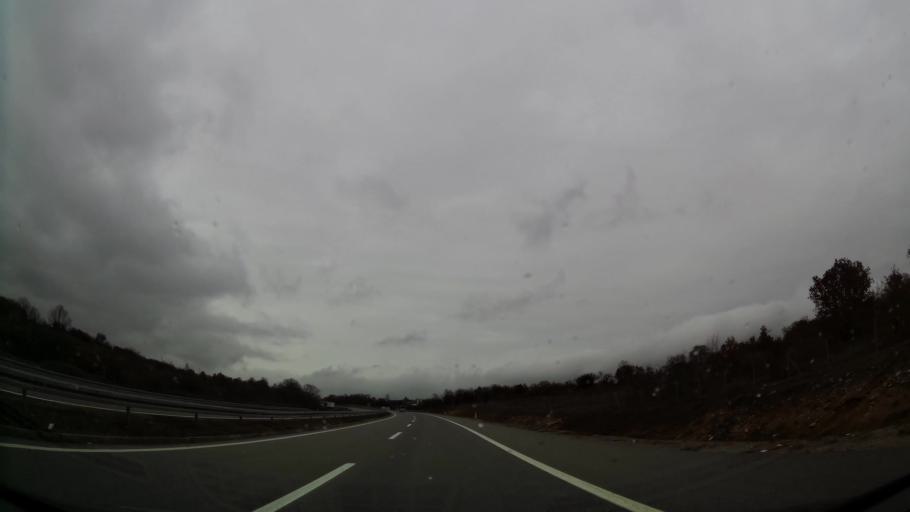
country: RS
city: Miratovac
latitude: 42.2693
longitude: 21.7031
